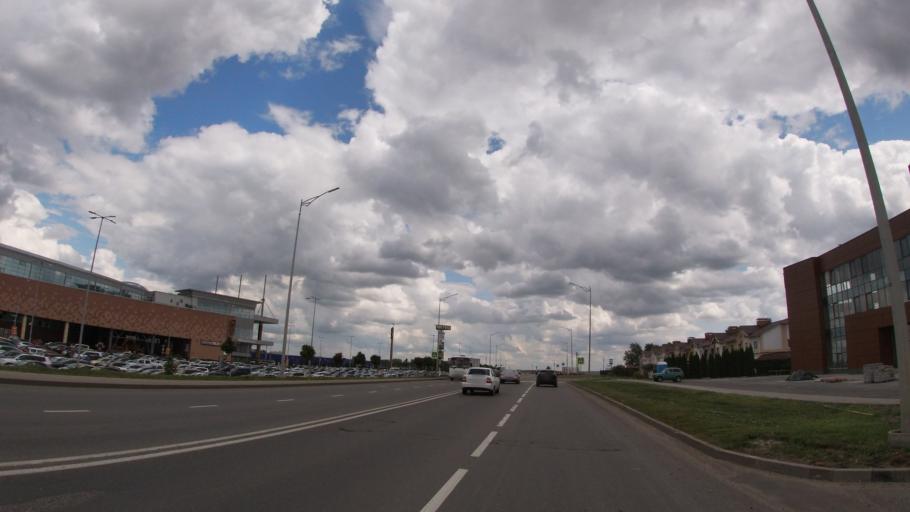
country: RU
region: Belgorod
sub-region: Belgorodskiy Rayon
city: Belgorod
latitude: 50.5511
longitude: 36.5691
